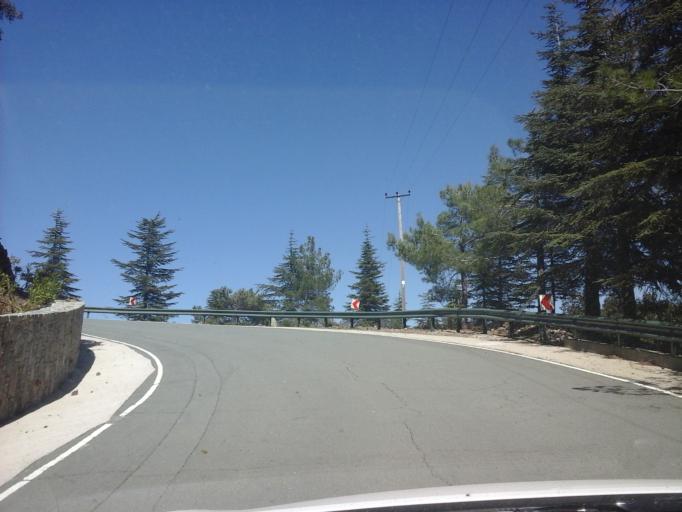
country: CY
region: Lefkosia
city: Kakopetria
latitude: 34.9856
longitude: 32.7420
